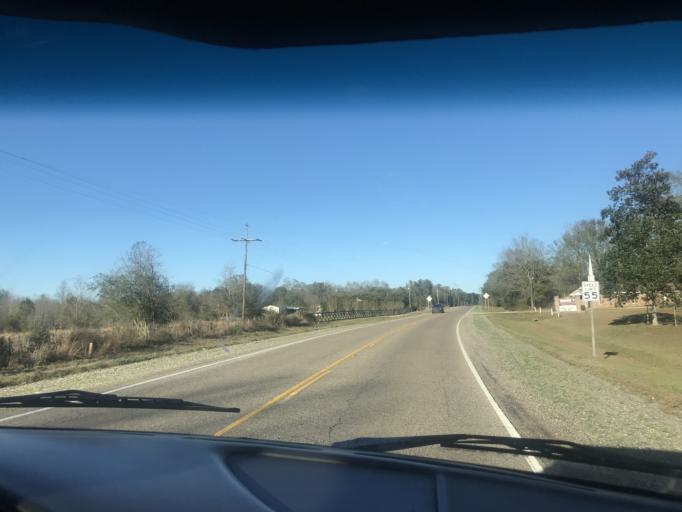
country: US
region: Louisiana
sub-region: Washington Parish
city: Franklinton
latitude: 30.6689
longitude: -90.2026
